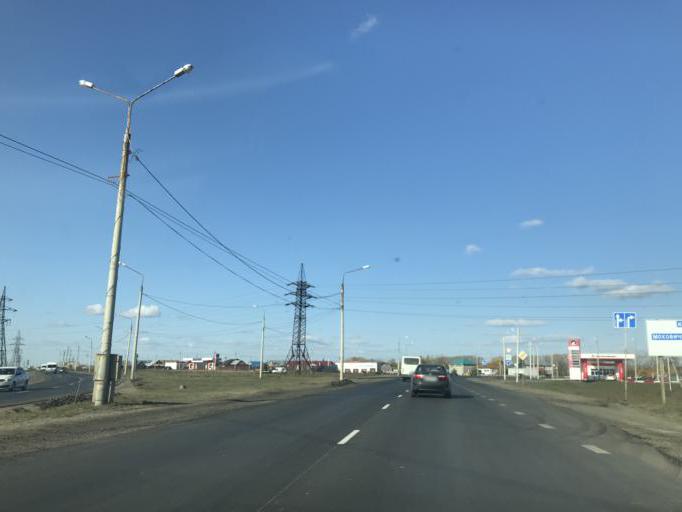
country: RU
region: Chelyabinsk
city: Roshchino
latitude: 55.2287
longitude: 61.2871
